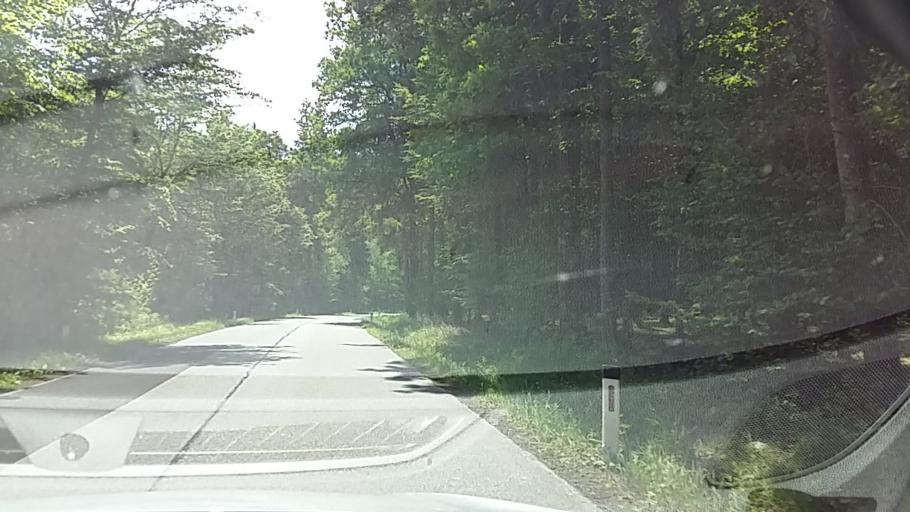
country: AT
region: Styria
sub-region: Politischer Bezirk Hartberg-Fuerstenfeld
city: Bad Blumau
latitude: 47.1190
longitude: 16.0197
